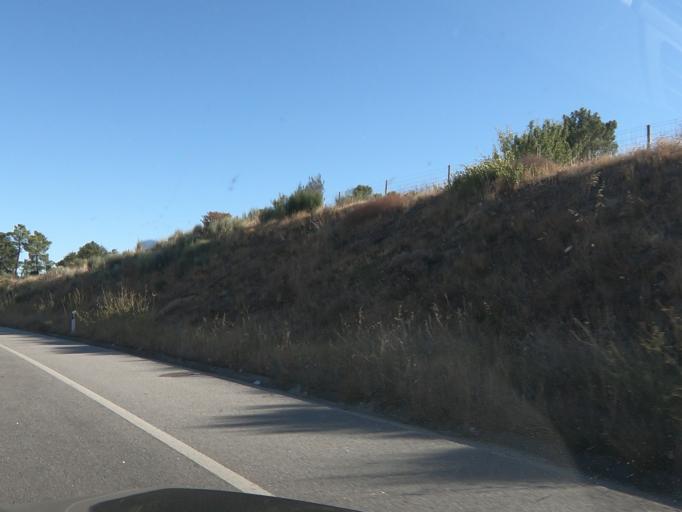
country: PT
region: Vila Real
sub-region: Valpacos
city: Valpacos
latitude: 41.5720
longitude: -7.2986
